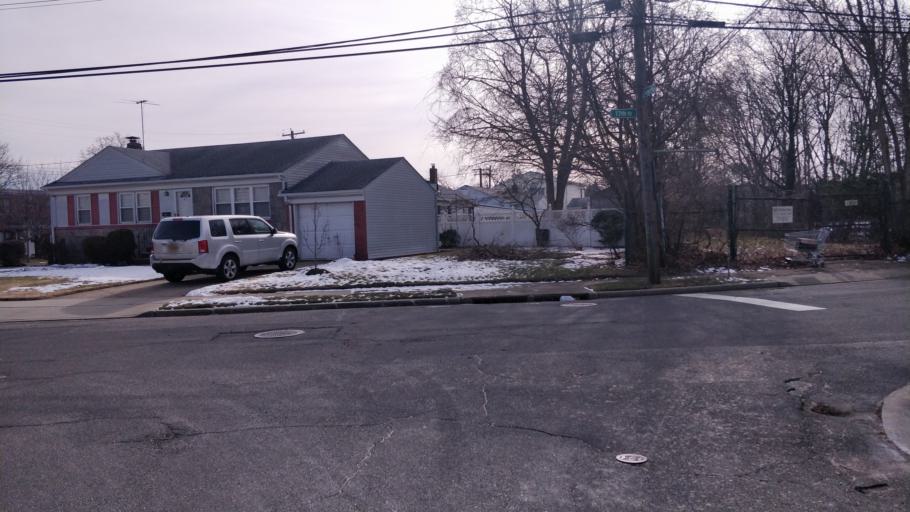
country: US
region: New York
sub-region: Nassau County
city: Jericho
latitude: 40.7791
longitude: -73.5361
